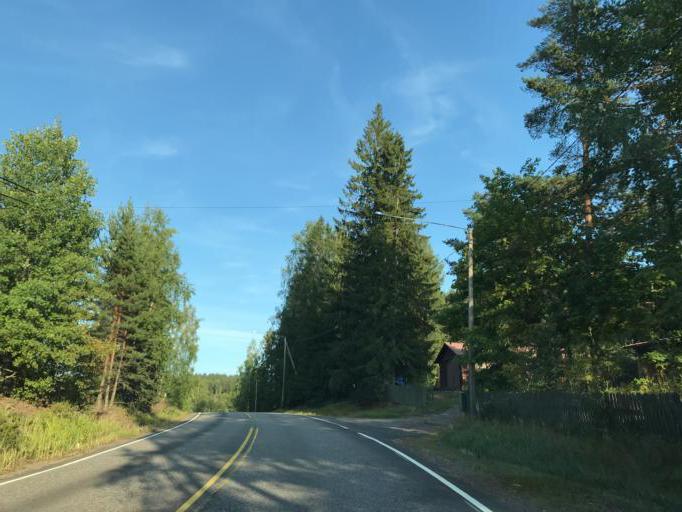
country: FI
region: Uusimaa
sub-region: Helsinki
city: Vihti
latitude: 60.4107
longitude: 24.4419
